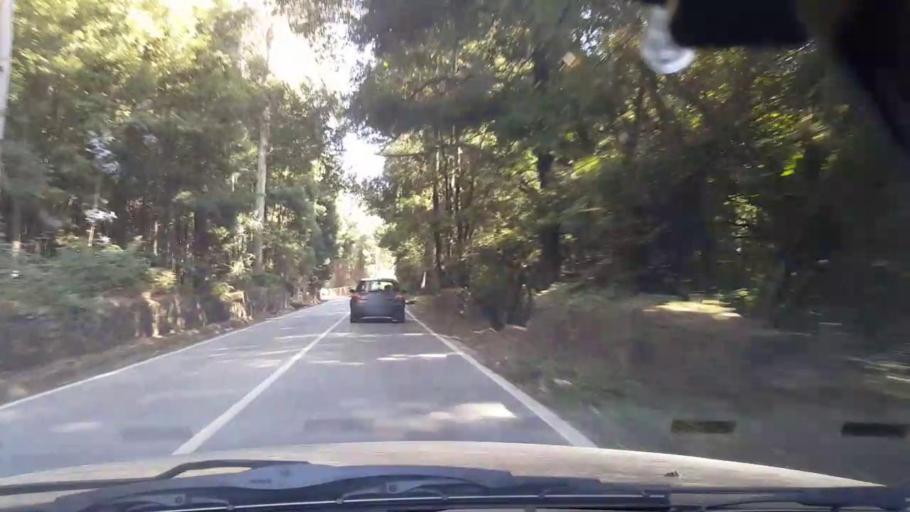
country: PT
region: Porto
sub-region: Maia
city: Gemunde
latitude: 41.3232
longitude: -8.6447
